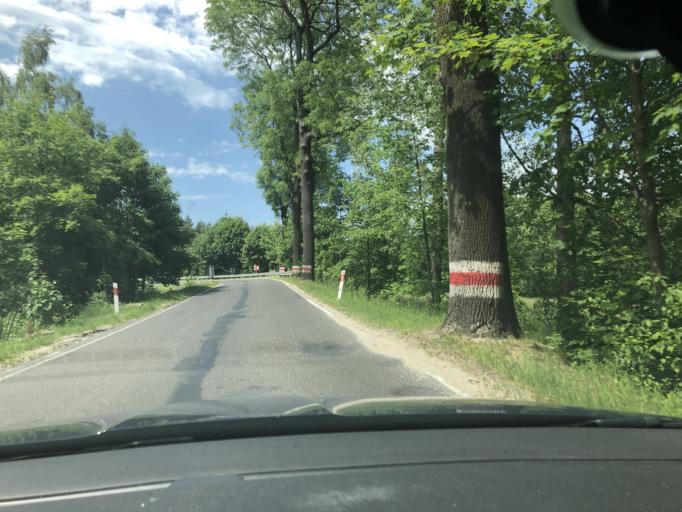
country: PL
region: Lower Silesian Voivodeship
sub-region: Powiat zlotoryjski
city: Swierzawa
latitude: 50.9663
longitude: 15.8303
